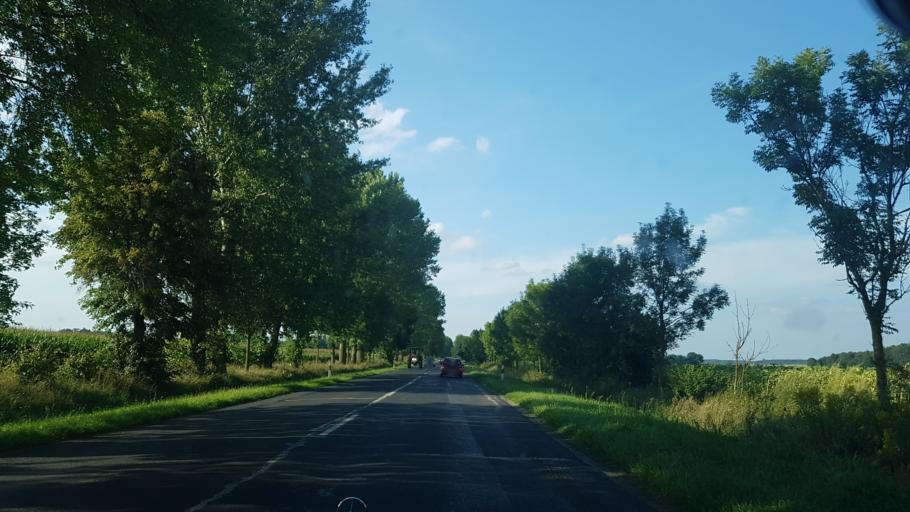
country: HU
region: Somogy
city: Nagyatad
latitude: 46.2576
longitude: 17.3569
